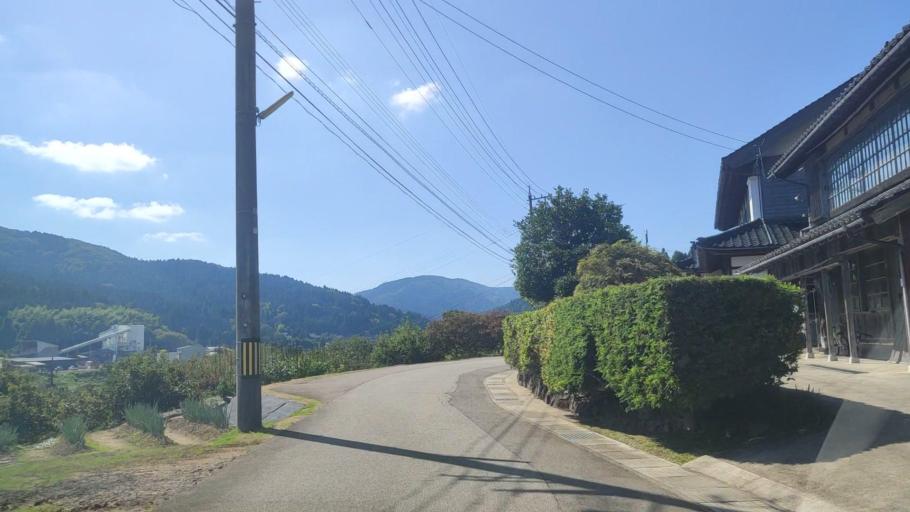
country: JP
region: Ishikawa
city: Nanao
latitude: 37.3700
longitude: 136.8694
